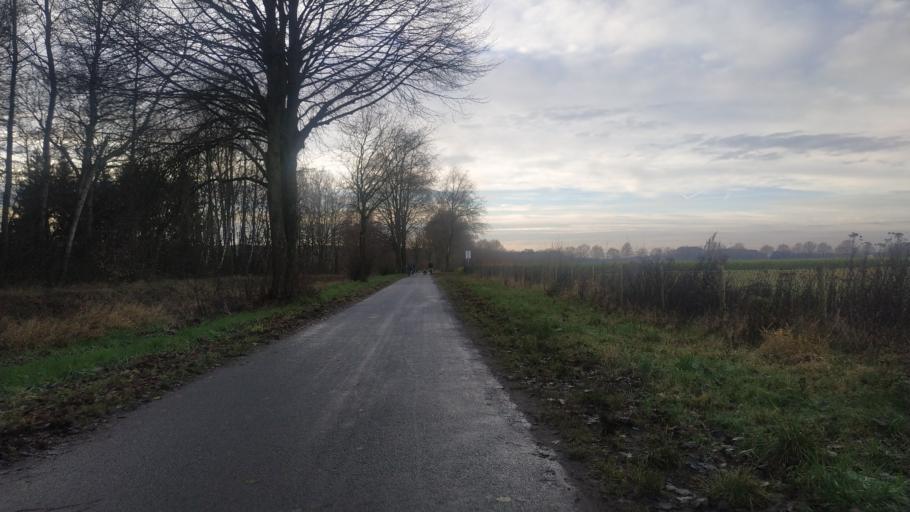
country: DE
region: North Rhine-Westphalia
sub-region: Regierungsbezirk Munster
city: Birgte
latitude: 52.2834
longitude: 7.6605
